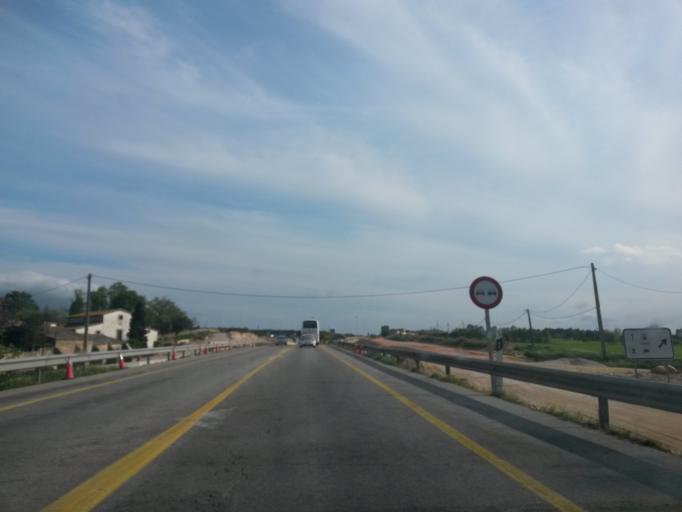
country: ES
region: Catalonia
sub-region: Provincia de Girona
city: Sils
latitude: 41.8094
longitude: 2.7640
